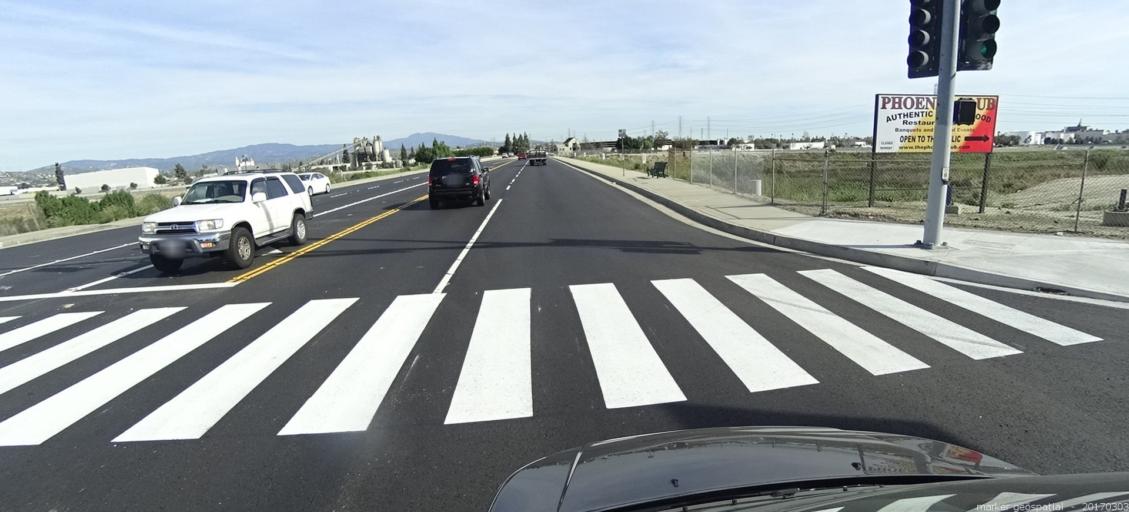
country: US
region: California
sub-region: Orange County
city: Orange
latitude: 33.8175
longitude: -117.8722
